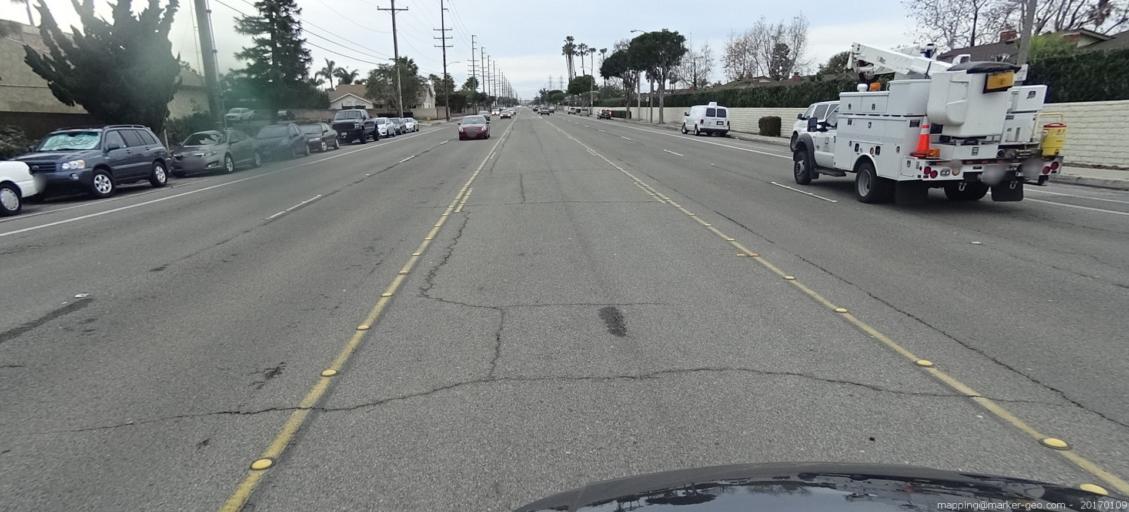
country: US
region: California
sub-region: Orange County
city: Costa Mesa
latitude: 33.6506
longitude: -117.9557
